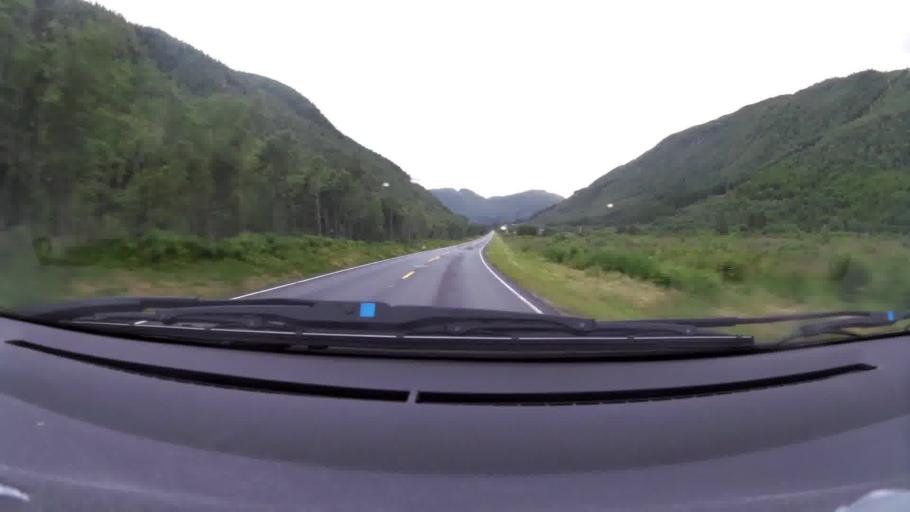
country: NO
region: More og Romsdal
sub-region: Molde
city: Molde
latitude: 62.7977
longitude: 7.3003
